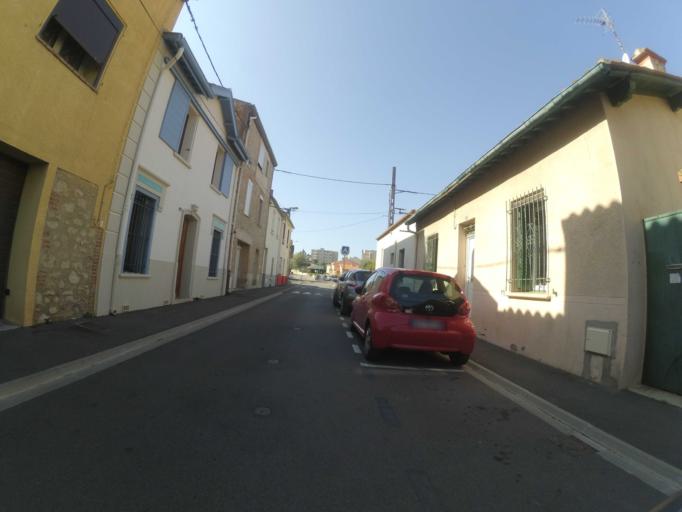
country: FR
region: Languedoc-Roussillon
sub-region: Departement des Pyrenees-Orientales
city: Thuir
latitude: 42.6310
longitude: 2.7534
